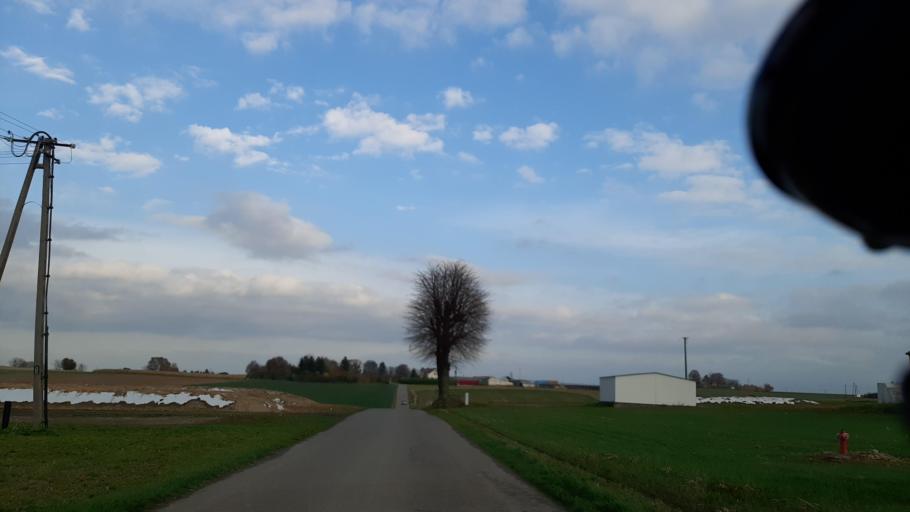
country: PL
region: Lublin Voivodeship
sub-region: Powiat pulawski
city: Markuszow
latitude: 51.3320
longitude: 22.2574
